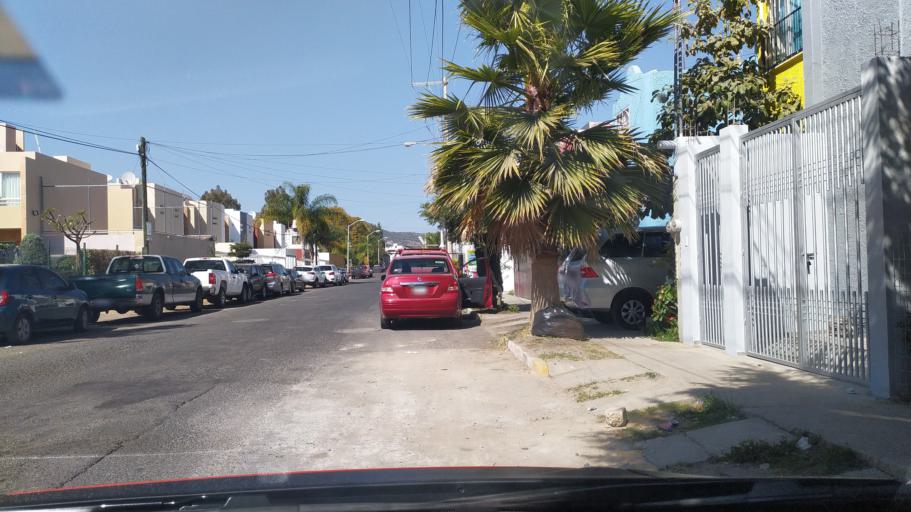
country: MX
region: Jalisco
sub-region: Tlajomulco de Zuniga
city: Palomar
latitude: 20.6287
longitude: -103.4624
